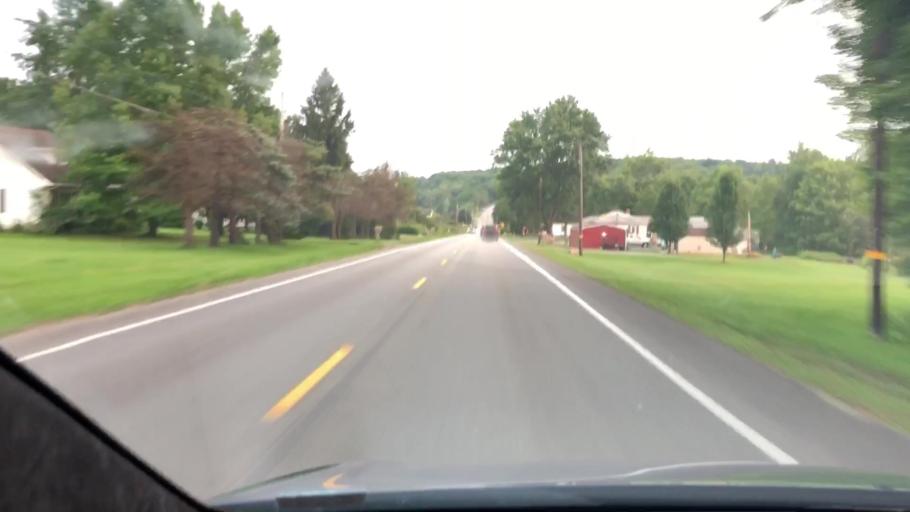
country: US
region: Pennsylvania
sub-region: Butler County
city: Slippery Rock
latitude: 41.0994
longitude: -80.0044
